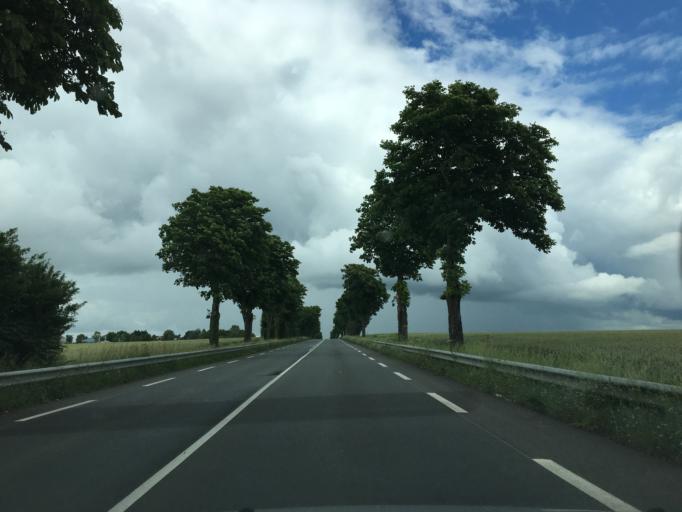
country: FR
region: Poitou-Charentes
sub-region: Departement des Deux-Sevres
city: Beauvoir-sur-Niort
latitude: 46.0798
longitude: -0.5058
